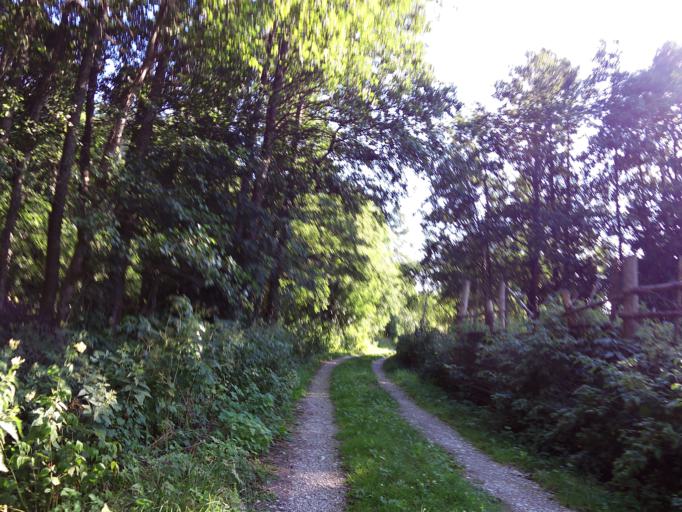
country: EE
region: Hiiumaa
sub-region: Kaerdla linn
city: Kardla
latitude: 58.8872
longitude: 22.2507
